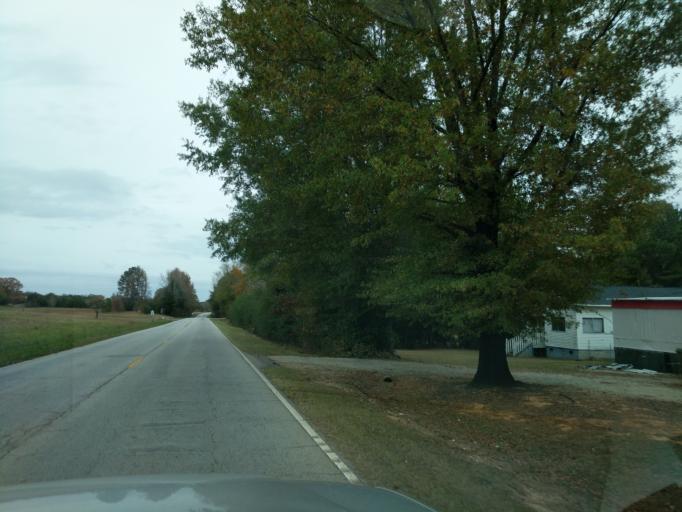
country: US
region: South Carolina
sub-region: Saluda County
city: Saluda
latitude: 34.0826
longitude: -81.7579
